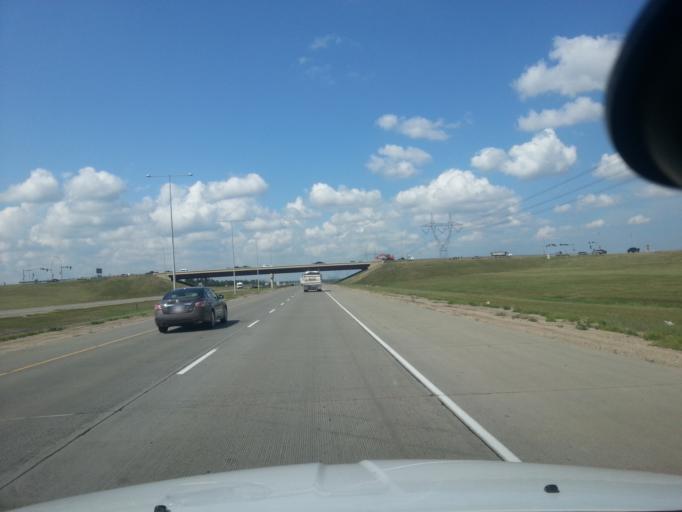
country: CA
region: Alberta
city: Devon
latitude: 53.4420
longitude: -113.5984
